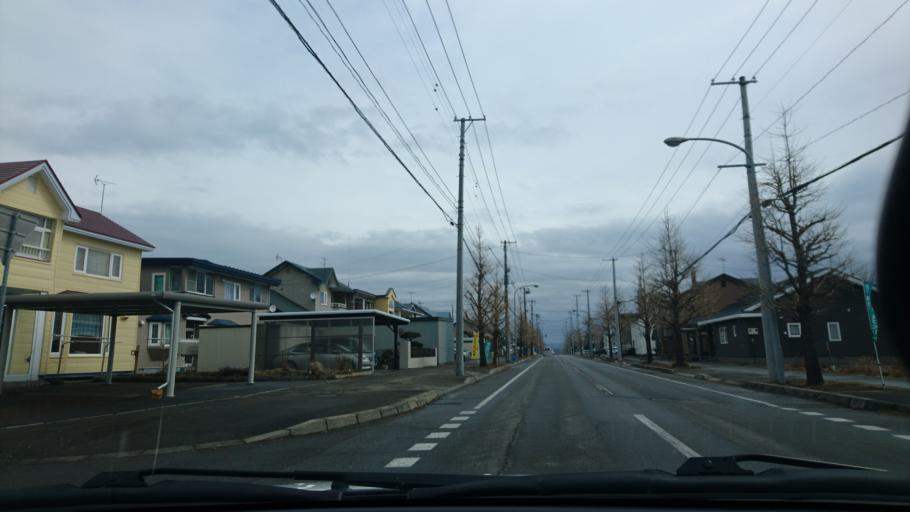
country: JP
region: Hokkaido
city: Otofuke
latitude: 42.9616
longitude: 143.1958
